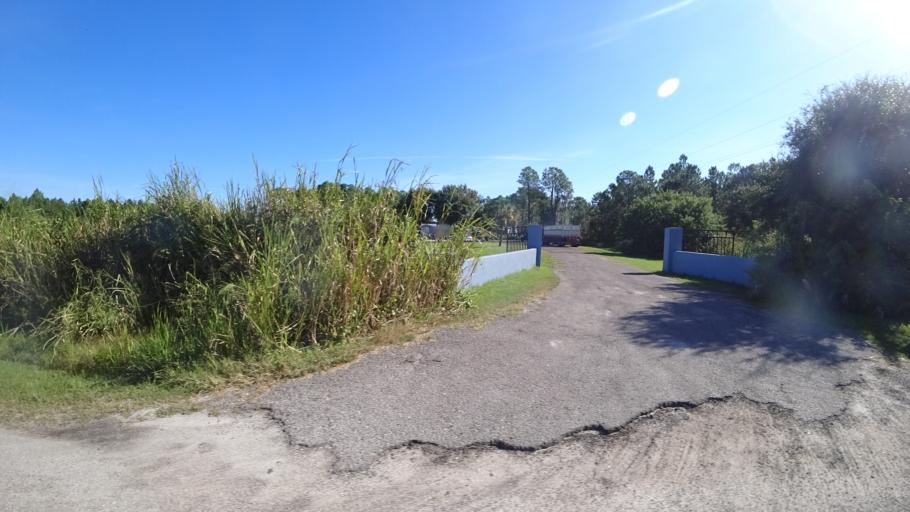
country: US
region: Florida
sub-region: Hillsborough County
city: Sun City Center
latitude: 27.6481
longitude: -82.3529
